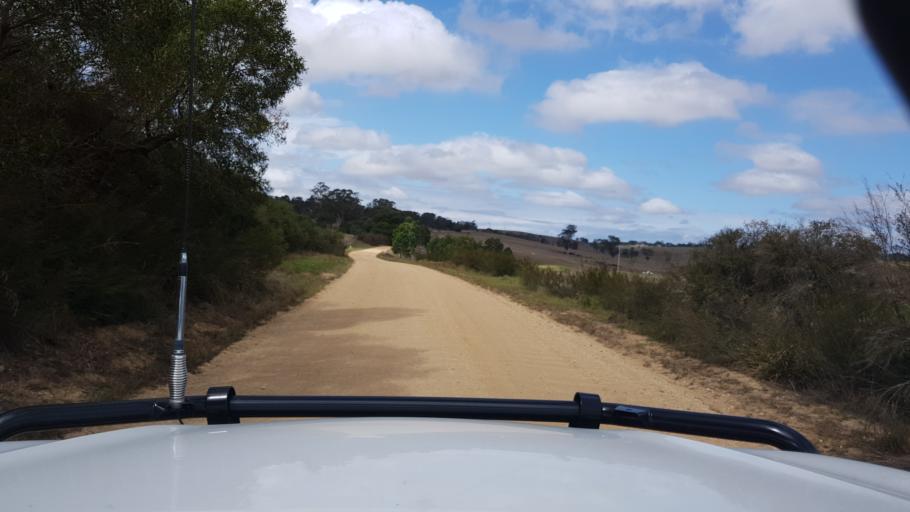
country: AU
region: Victoria
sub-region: East Gippsland
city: Bairnsdale
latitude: -37.7849
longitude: 147.5528
